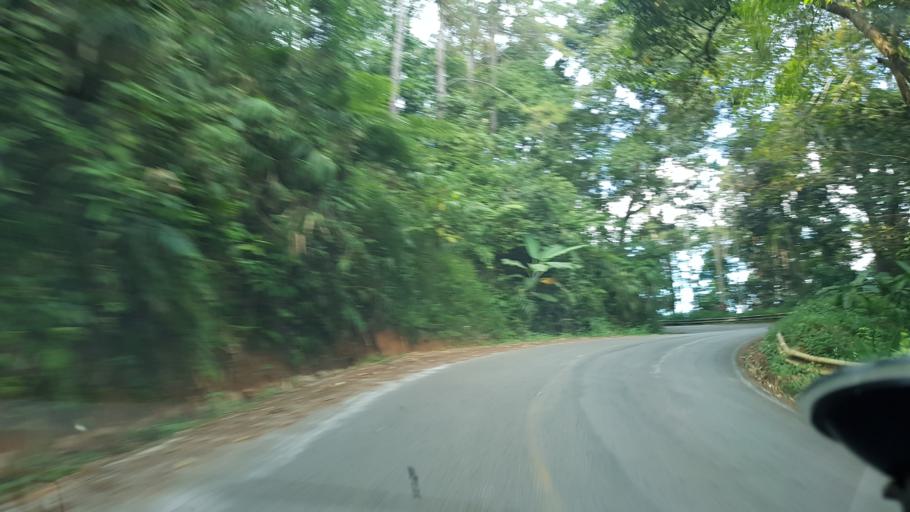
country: TH
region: Chiang Rai
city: Mae Fa Luang
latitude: 20.3272
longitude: 99.8200
